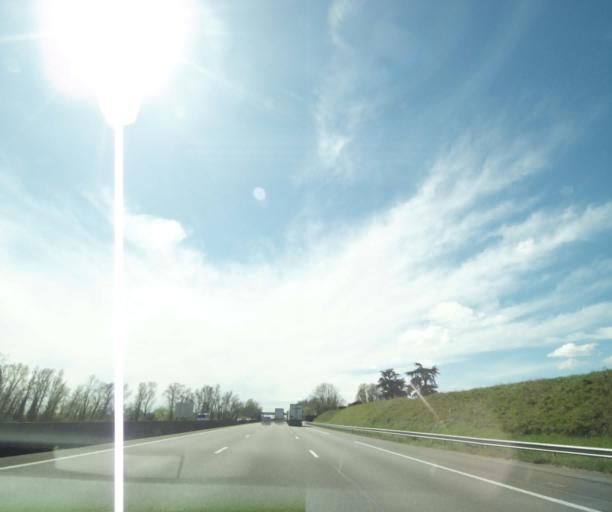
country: FR
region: Rhone-Alpes
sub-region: Departement du Rhone
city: Saint-Georges-de-Reneins
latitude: 46.0754
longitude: 4.7415
